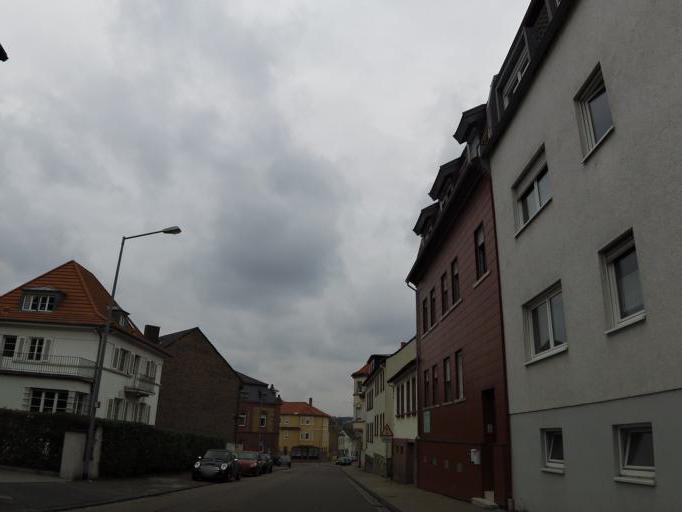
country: DE
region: Saarland
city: Sankt Ingbert
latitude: 49.2734
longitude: 7.1123
